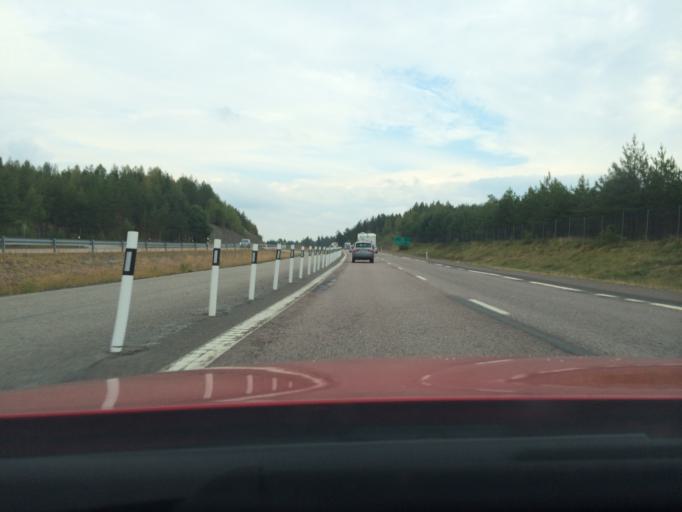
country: SE
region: Soedermanland
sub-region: Nykopings Kommun
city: Olstorp
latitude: 58.7548
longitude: 16.6402
